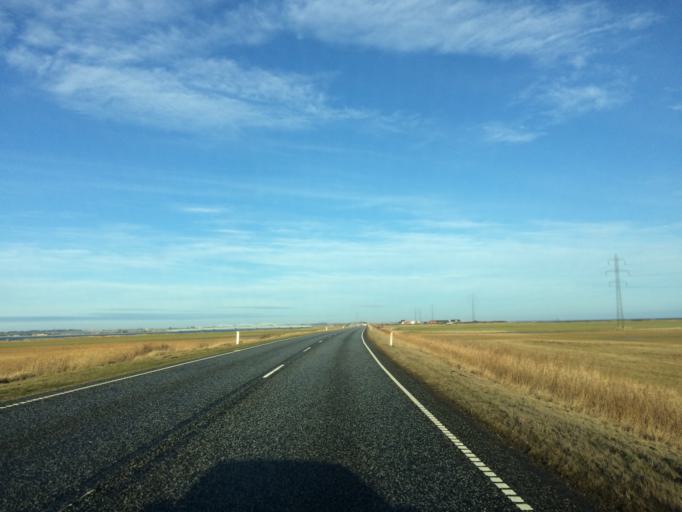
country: DK
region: Central Jutland
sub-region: Struer Kommune
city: Struer
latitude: 56.5618
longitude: 8.5577
